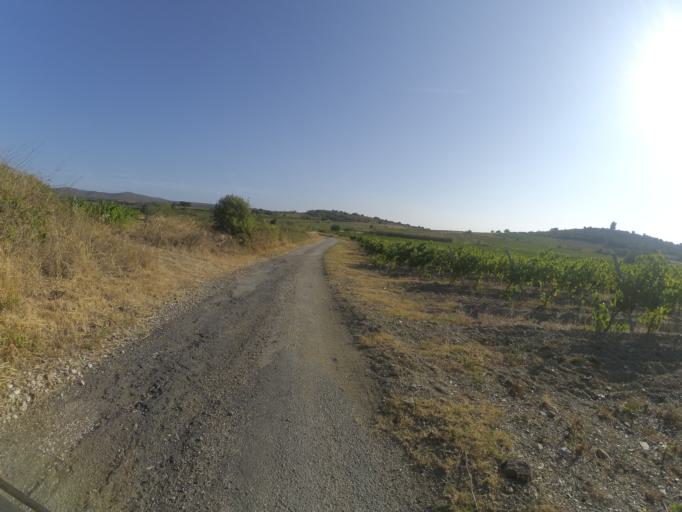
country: FR
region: Languedoc-Roussillon
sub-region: Departement des Pyrenees-Orientales
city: Baixas
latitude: 42.7415
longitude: 2.7802
